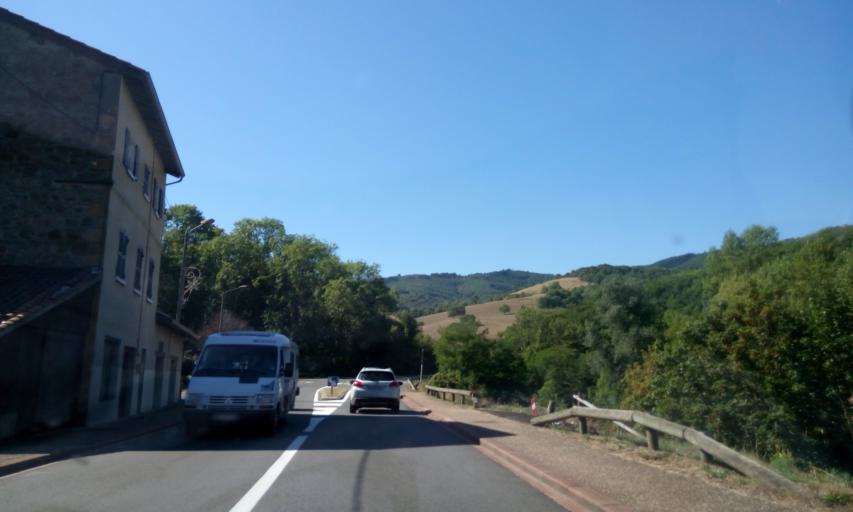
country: FR
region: Rhone-Alpes
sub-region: Departement du Rhone
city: Saint-Verand
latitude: 45.9811
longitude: 4.5084
